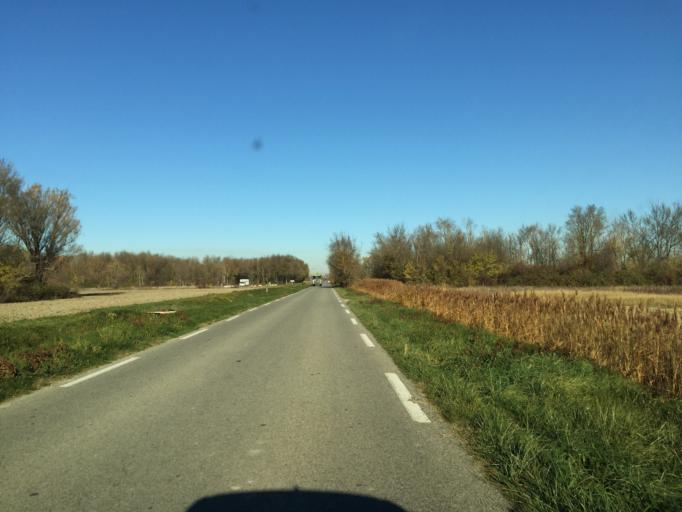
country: FR
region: Provence-Alpes-Cote d'Azur
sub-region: Departement du Vaucluse
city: Entraigues-sur-la-Sorgue
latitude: 44.0238
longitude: 4.9171
